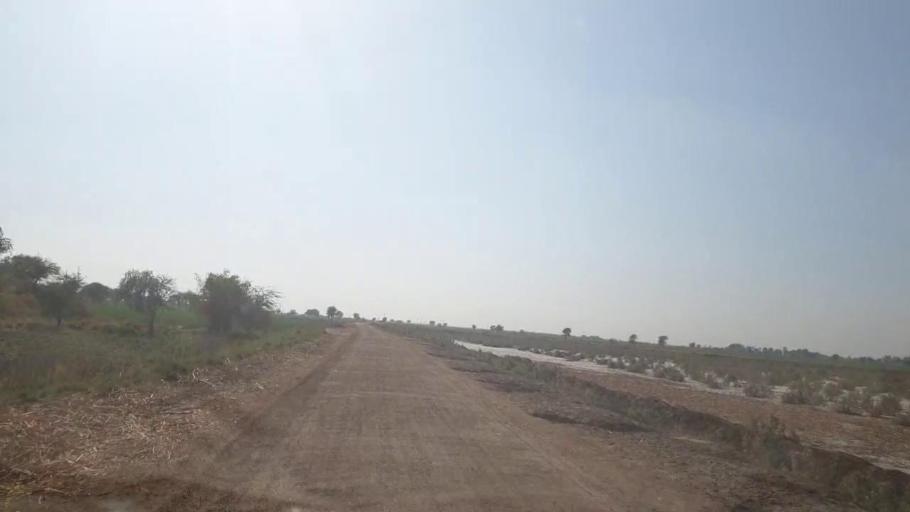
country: PK
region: Sindh
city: Mirpur Khas
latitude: 25.4538
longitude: 69.1178
